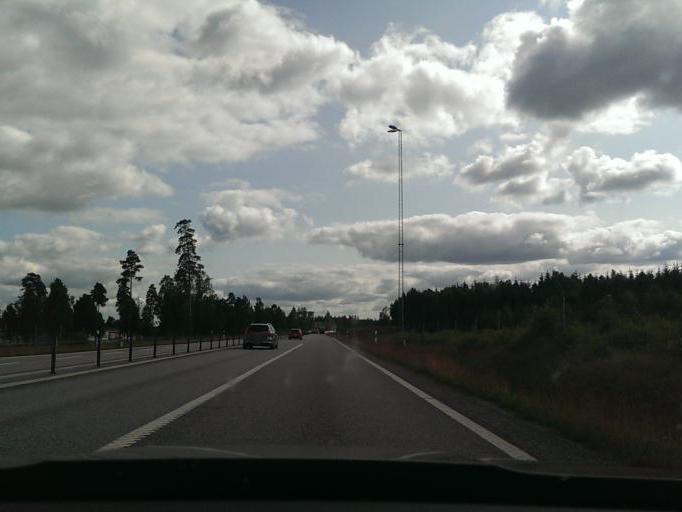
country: SE
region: Kronoberg
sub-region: Ljungby Kommun
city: Lagan
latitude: 56.9159
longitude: 13.9726
